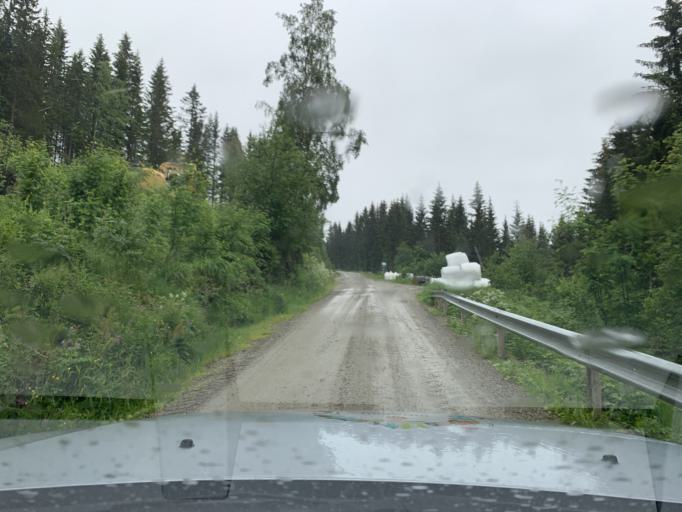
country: NO
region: Oppland
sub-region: Oyer
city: Tretten
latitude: 61.3859
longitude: 10.2836
